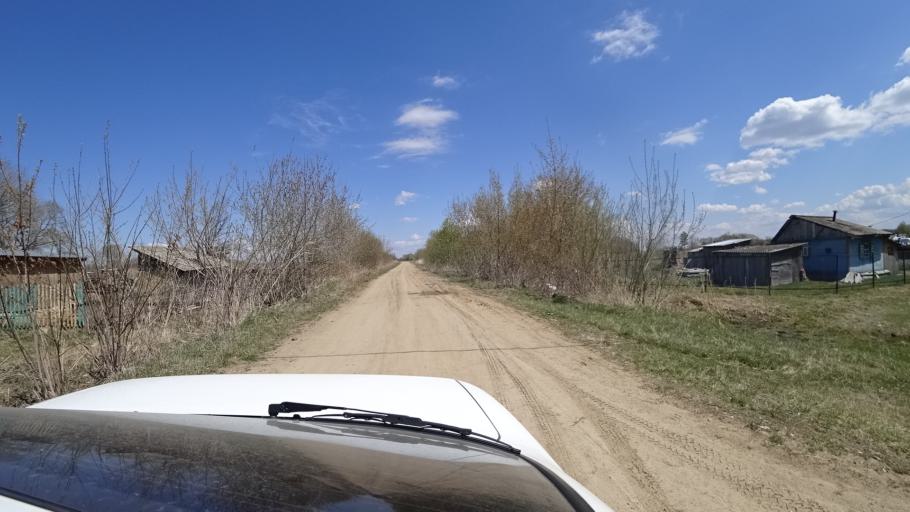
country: RU
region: Primorskiy
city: Dal'nerechensk
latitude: 45.7999
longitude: 133.7689
